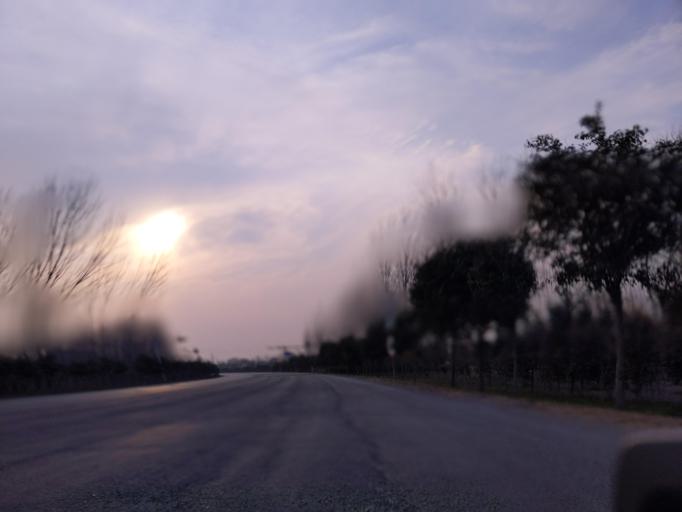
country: CN
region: Henan Sheng
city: Puyang
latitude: 35.8202
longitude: 114.9781
